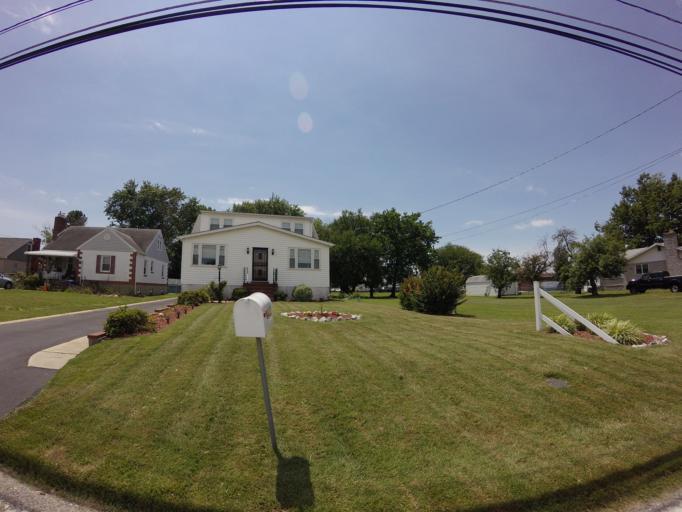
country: US
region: Maryland
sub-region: Baltimore County
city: Edgemere
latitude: 39.2661
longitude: -76.4655
